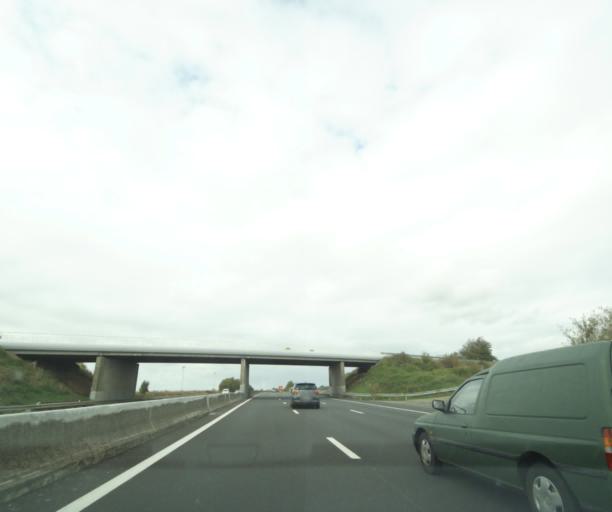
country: FR
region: Centre
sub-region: Departement d'Eure-et-Loir
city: Janville
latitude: 48.3219
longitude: 1.8635
